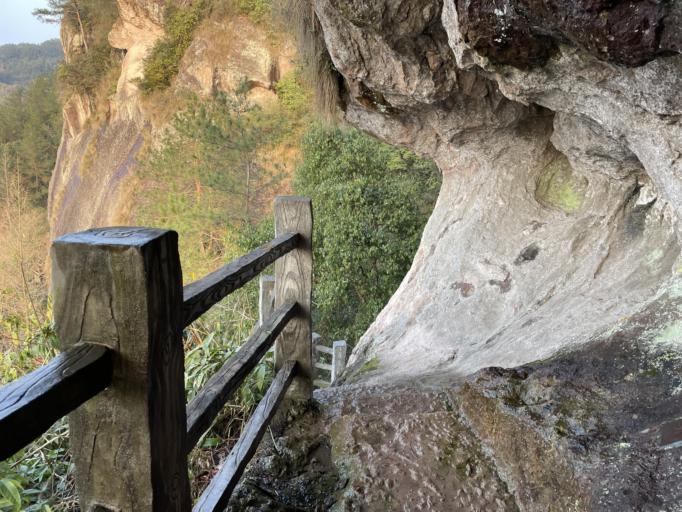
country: CN
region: Zhejiang Sheng
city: Shuhong
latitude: 28.6864
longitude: 120.1209
